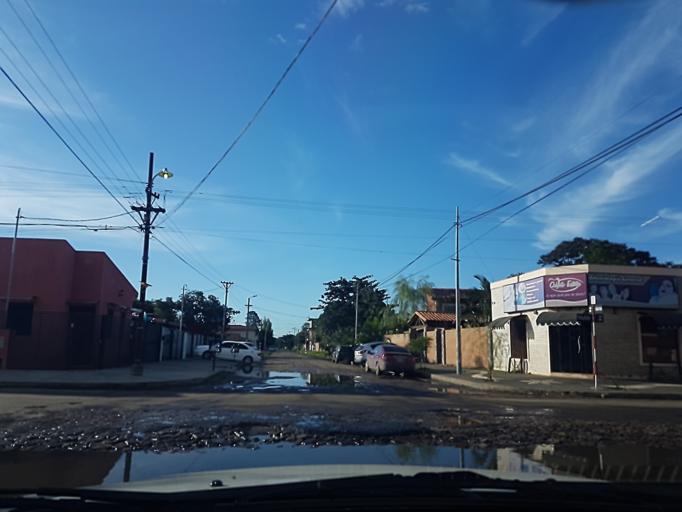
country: PY
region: Central
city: Colonia Mariano Roque Alonso
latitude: -25.2111
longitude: -57.5367
